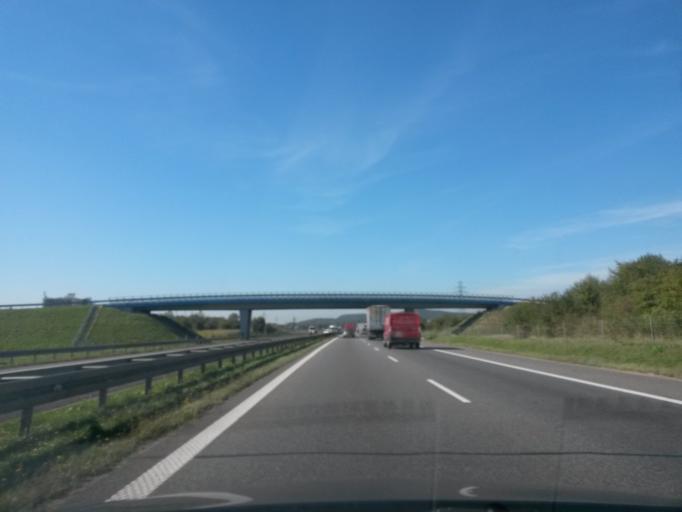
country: PL
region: Lesser Poland Voivodeship
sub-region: Krakow
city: Sidzina
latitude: 49.9922
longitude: 19.8767
